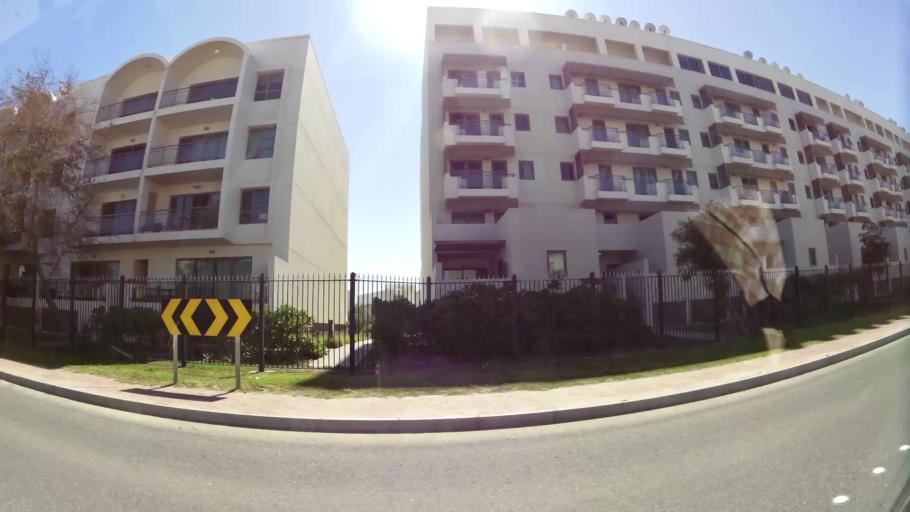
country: BH
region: Muharraq
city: Al Hadd
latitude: 26.3002
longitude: 50.6637
